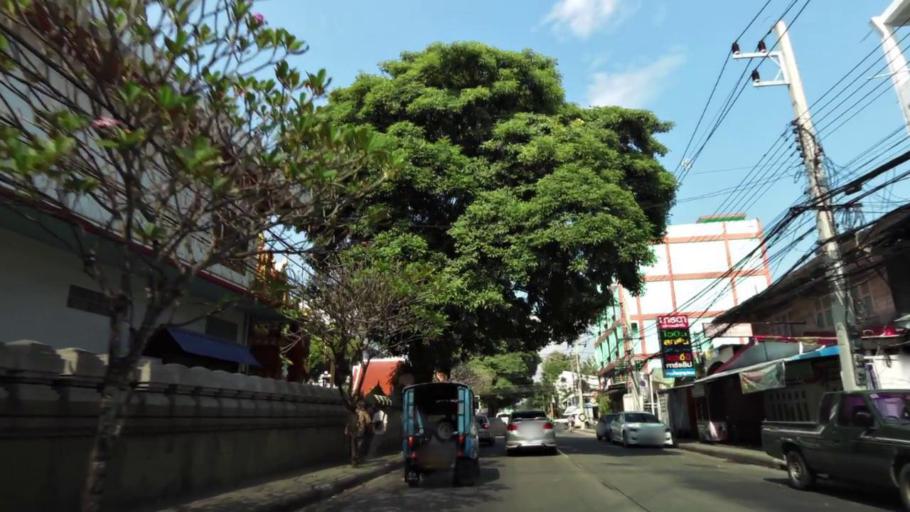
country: TH
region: Chiang Rai
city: Chiang Rai
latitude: 19.9106
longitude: 99.8328
